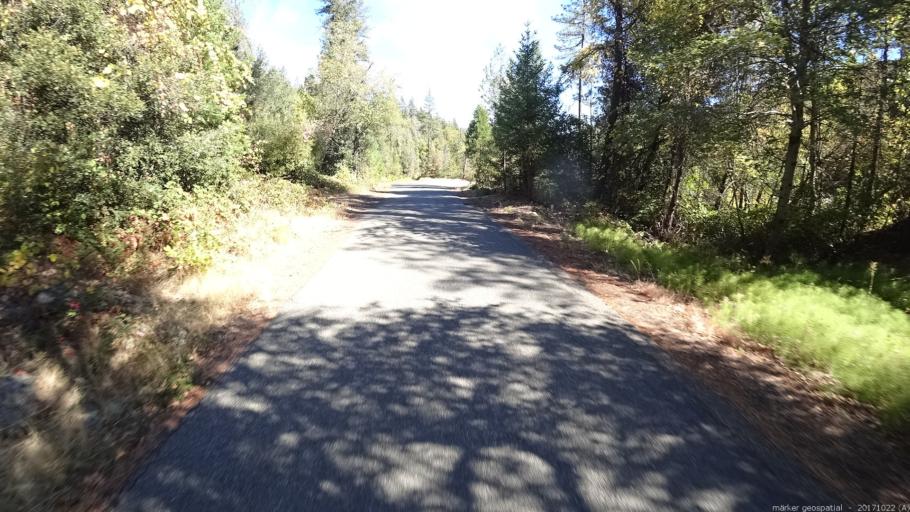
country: US
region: California
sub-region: Shasta County
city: Central Valley (historical)
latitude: 40.9352
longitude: -122.4581
